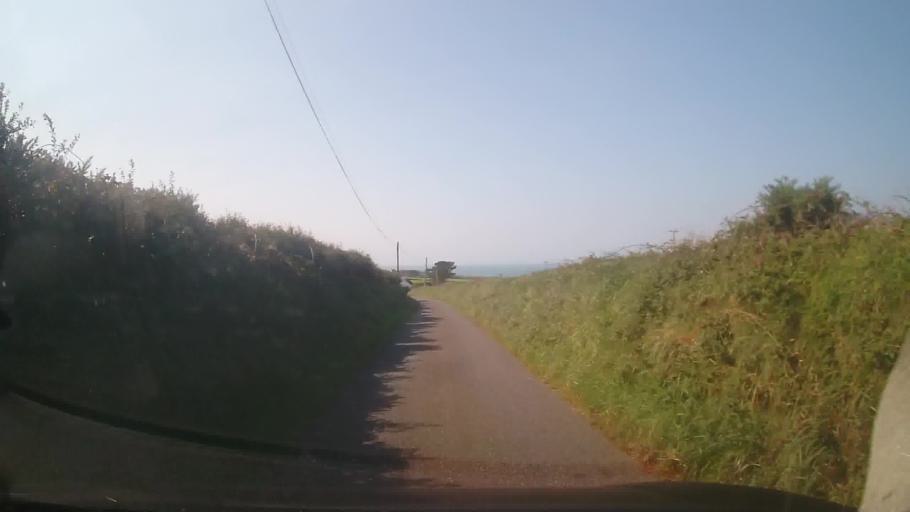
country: GB
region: Wales
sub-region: Pembrokeshire
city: Llanrhian
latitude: 51.9291
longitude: -5.1895
